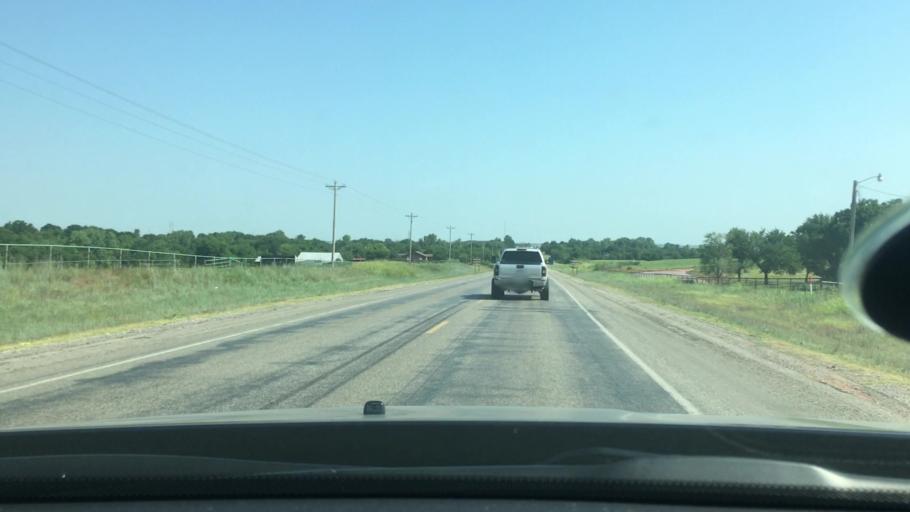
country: US
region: Oklahoma
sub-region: Garvin County
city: Lindsay
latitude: 34.7832
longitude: -97.5982
